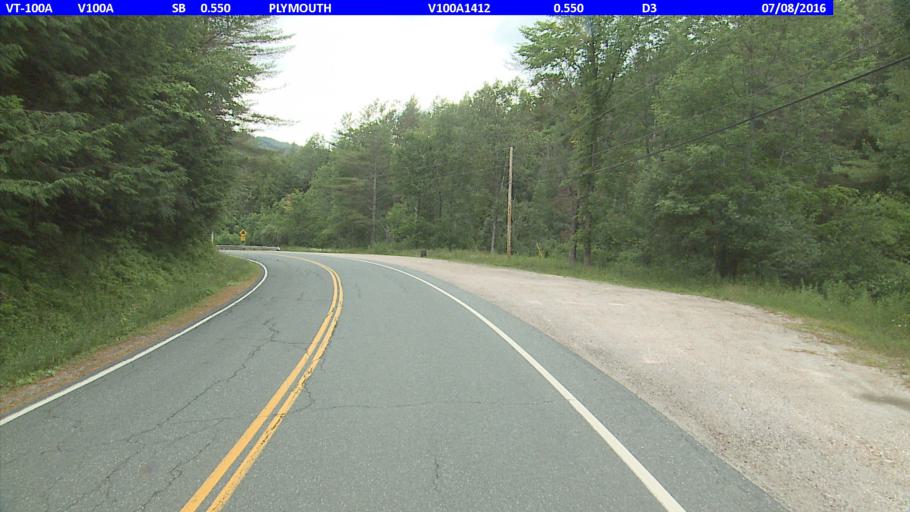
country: US
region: Vermont
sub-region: Windsor County
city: Woodstock
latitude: 43.5340
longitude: -72.7301
